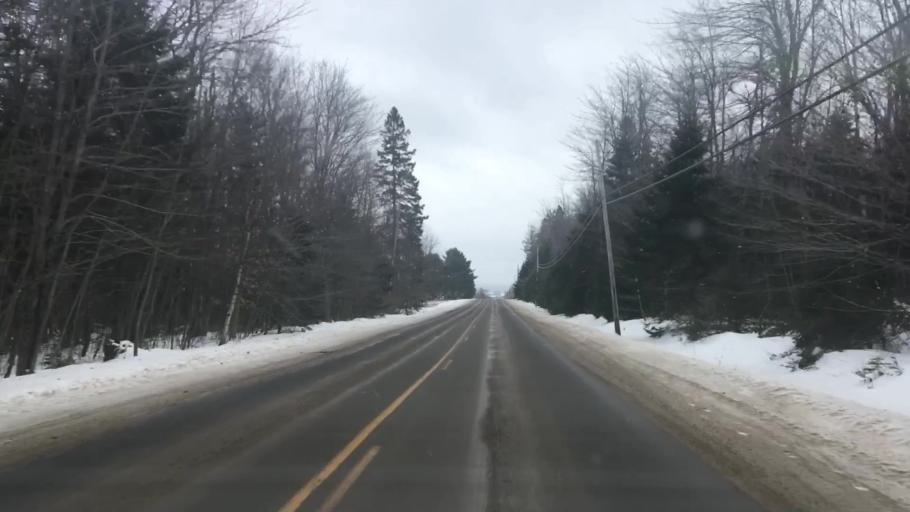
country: US
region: Maine
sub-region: Washington County
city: East Machias
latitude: 44.9833
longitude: -67.4556
